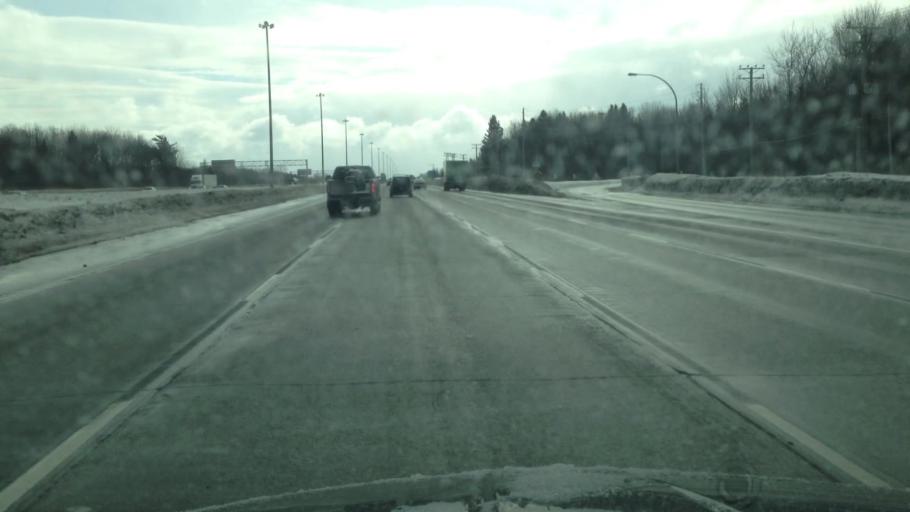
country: CA
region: Quebec
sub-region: Laurentides
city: Blainville
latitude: 45.6570
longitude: -73.8842
